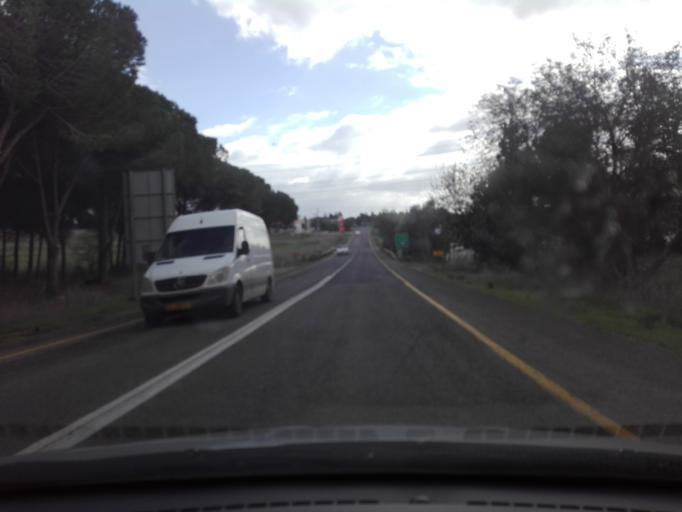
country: IL
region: Haifa
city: Daliyat el Karmil
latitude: 32.6402
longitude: 35.0599
